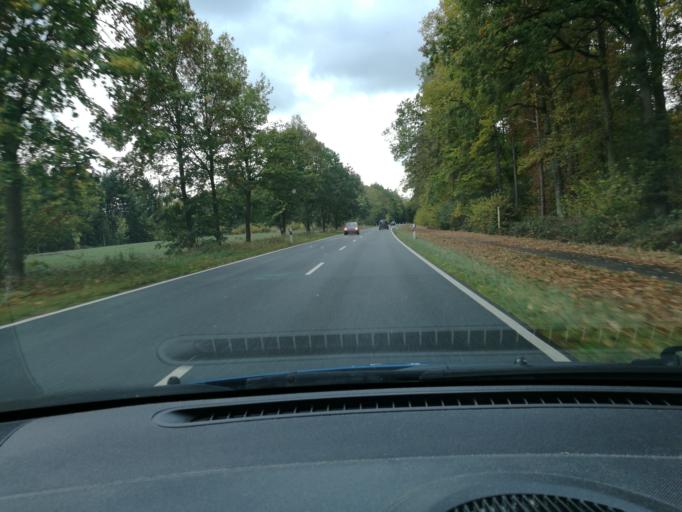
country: DE
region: Schleswig-Holstein
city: Gross Gronau
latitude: 53.7830
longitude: 10.7533
